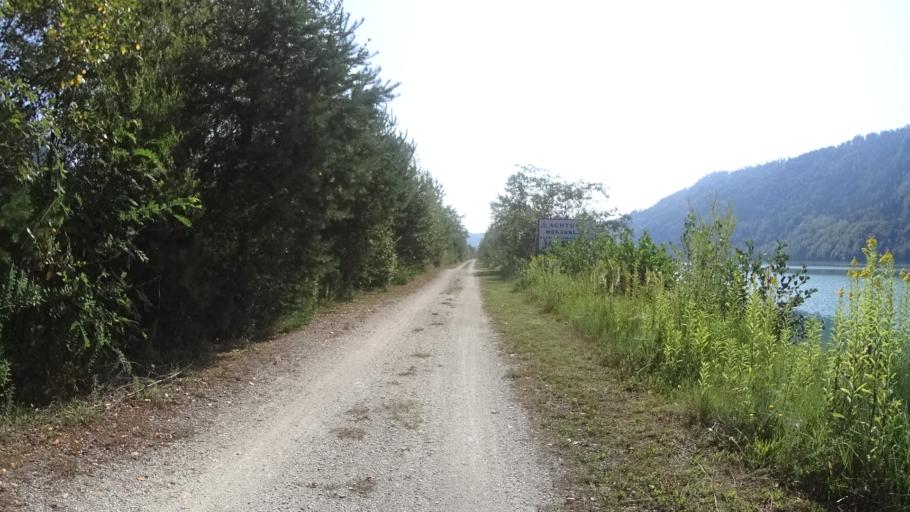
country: AT
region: Carinthia
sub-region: Politischer Bezirk Klagenfurt Land
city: Grafenstein
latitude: 46.5631
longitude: 14.4662
